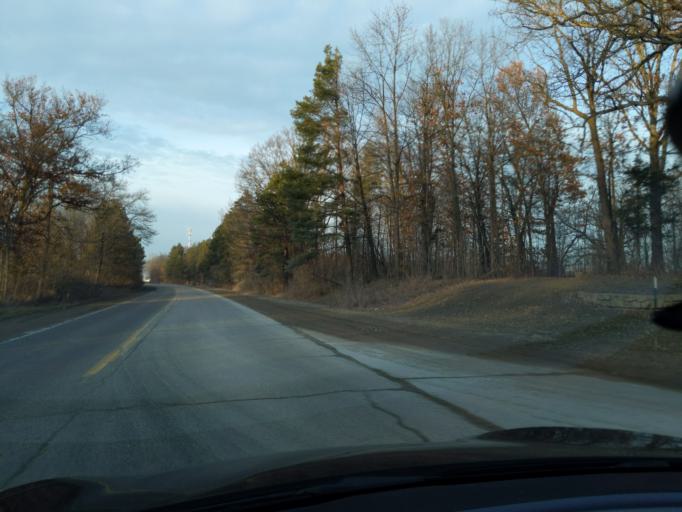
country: US
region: Michigan
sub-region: Livingston County
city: Brighton
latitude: 42.6112
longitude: -83.7479
